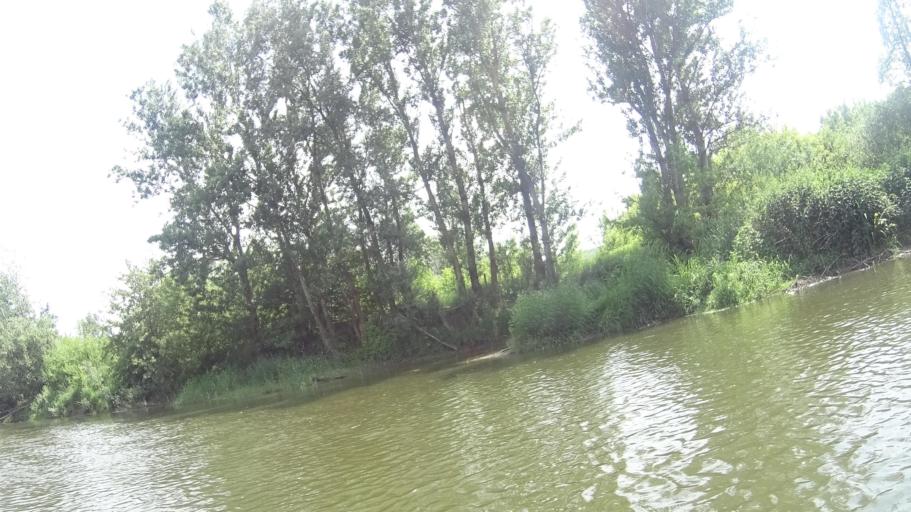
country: HU
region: Komarom-Esztergom
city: Esztergom
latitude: 47.8688
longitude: 18.7753
